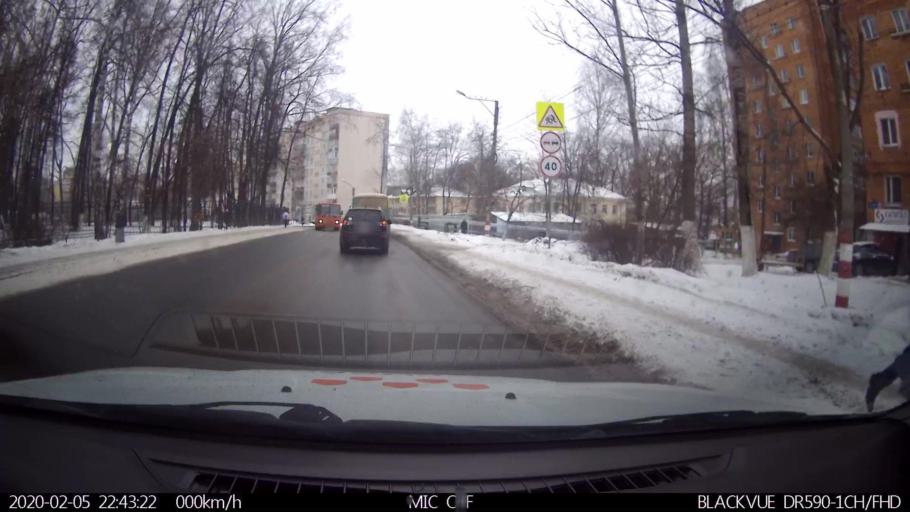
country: RU
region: Nizjnij Novgorod
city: Imeni Stepana Razina
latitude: 54.7131
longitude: 44.3754
